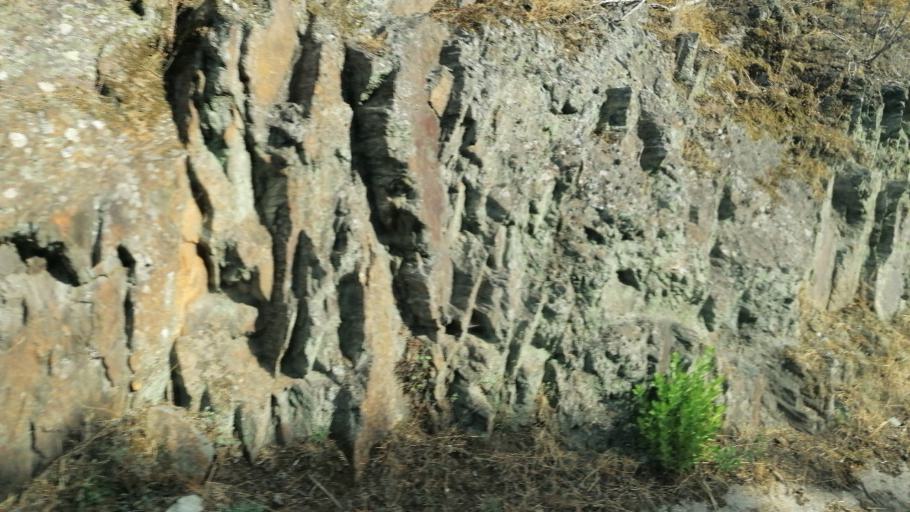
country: PT
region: Viseu
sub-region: Sao Joao da Pesqueira
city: Sao Joao da Pesqueira
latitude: 41.1136
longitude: -7.4574
